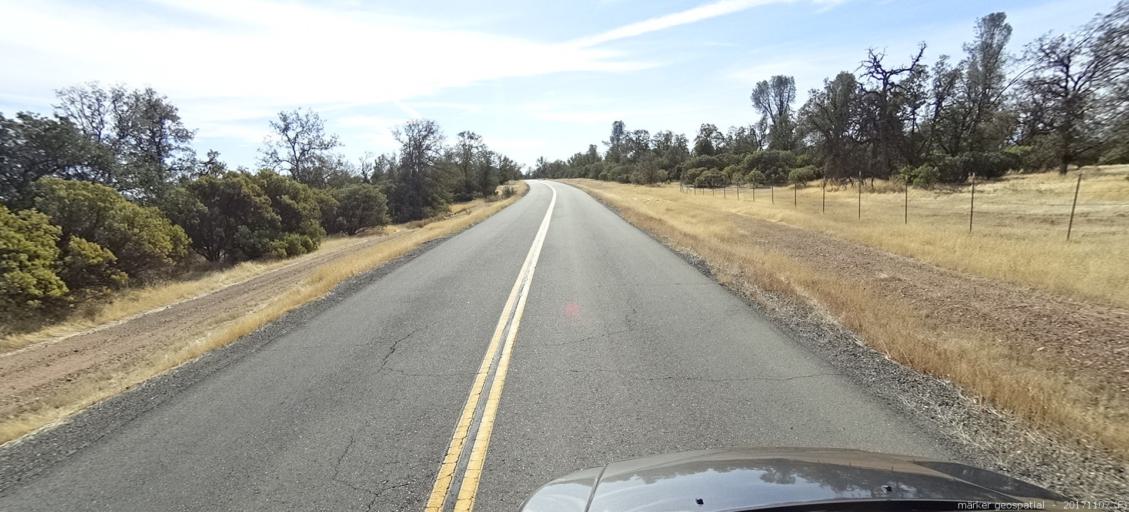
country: US
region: California
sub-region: Shasta County
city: Shasta
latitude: 40.4773
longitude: -122.5444
